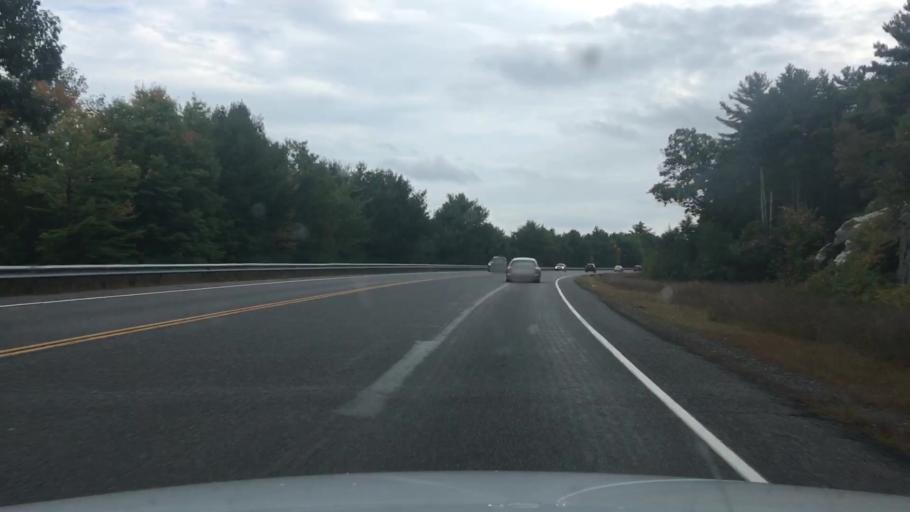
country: US
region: New Hampshire
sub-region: Carroll County
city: Wolfeboro
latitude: 43.5330
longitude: -71.2760
